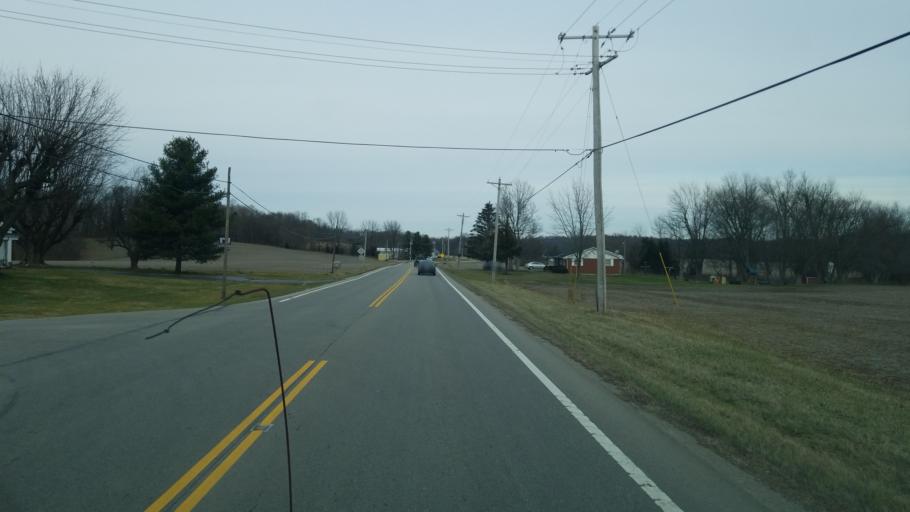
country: US
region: Ohio
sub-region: Highland County
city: Hillsboro
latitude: 39.1479
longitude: -83.6644
